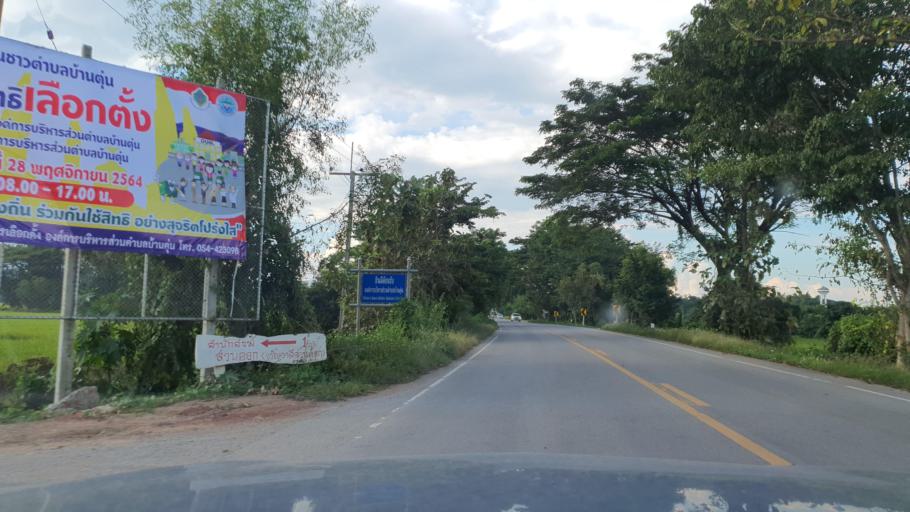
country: TH
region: Phayao
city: Phayao
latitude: 19.1279
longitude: 99.8432
